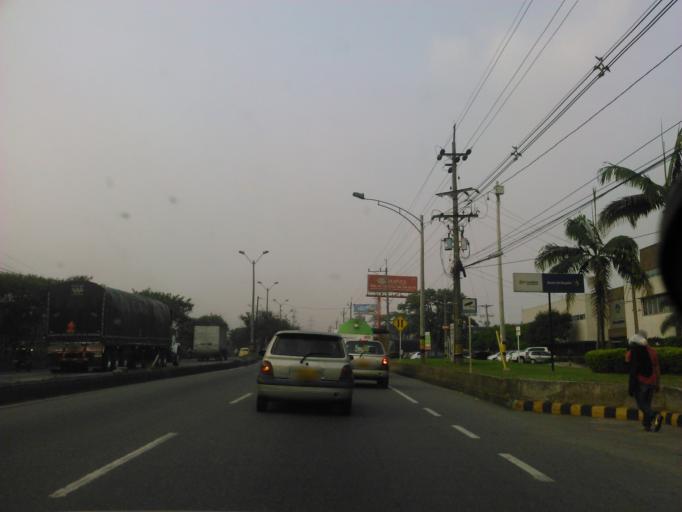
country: CO
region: Antioquia
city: Envigado
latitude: 6.1822
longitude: -75.5905
